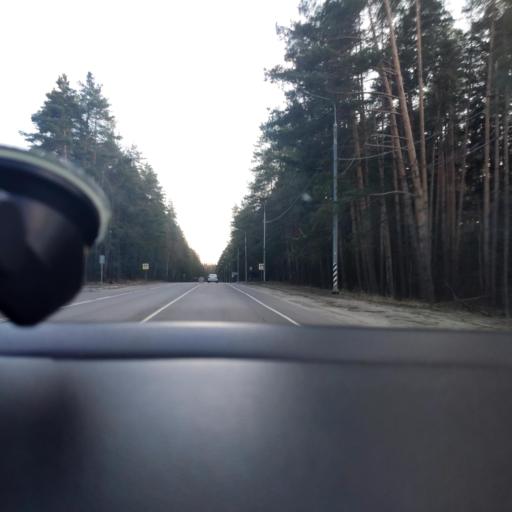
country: RU
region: Moskovskaya
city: Krasnyy Tkach
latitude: 55.4150
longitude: 39.1748
